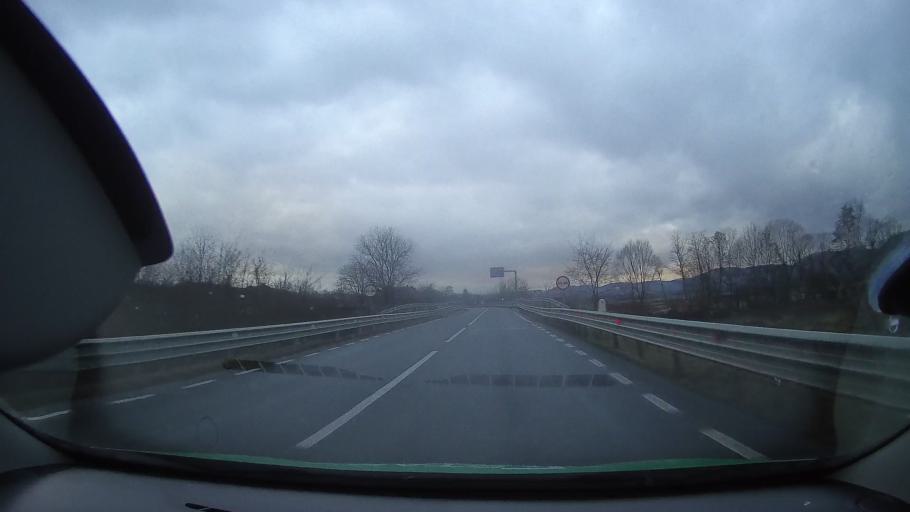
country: RO
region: Hunedoara
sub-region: Comuna Baia de Cris
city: Baia de Cris
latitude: 46.1701
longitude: 22.7265
